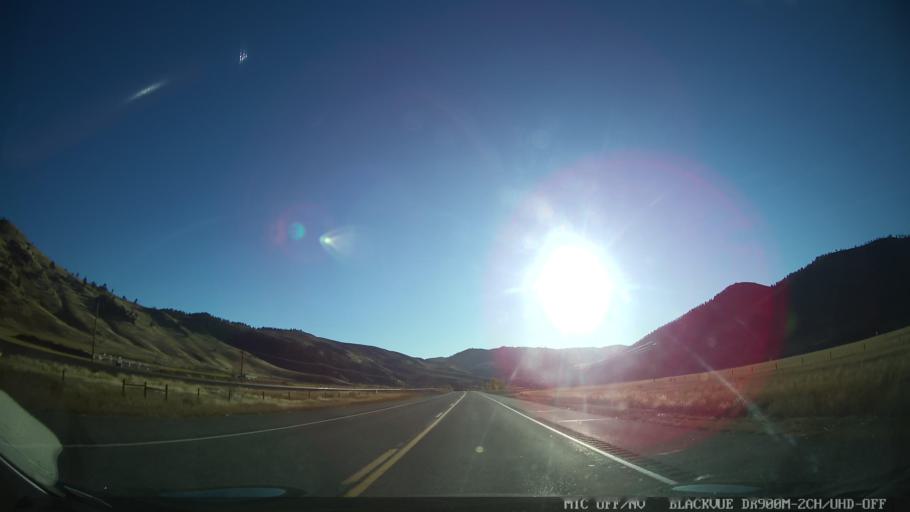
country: US
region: Colorado
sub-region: Grand County
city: Hot Sulphur Springs
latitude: 40.0508
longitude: -106.1443
